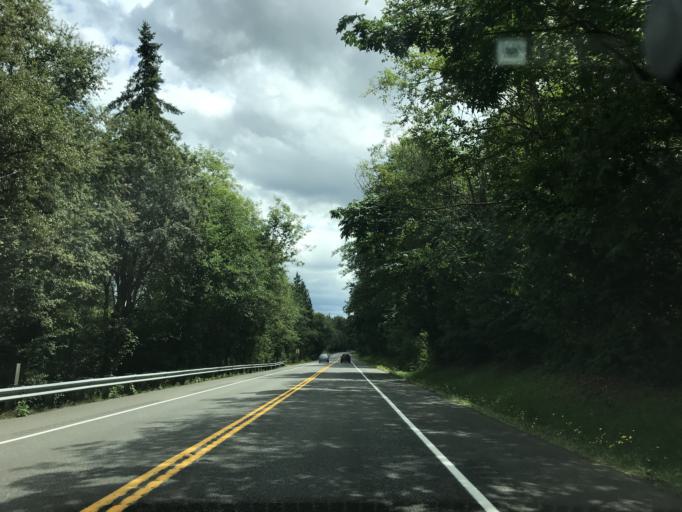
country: US
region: Washington
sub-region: King County
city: Maple Valley
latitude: 47.4144
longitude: -122.0622
